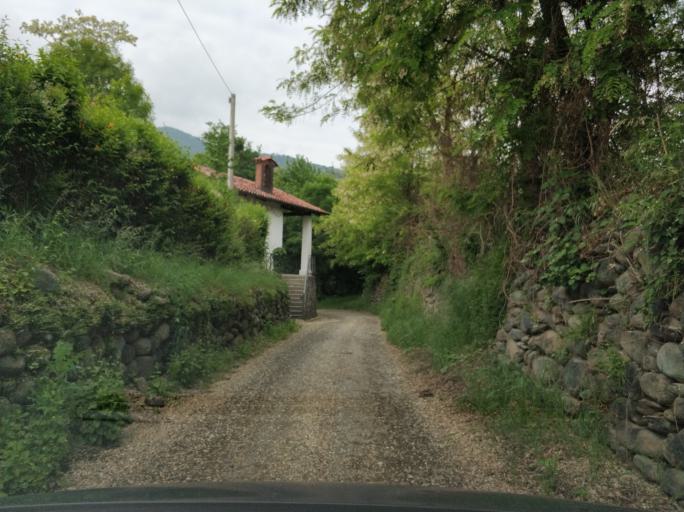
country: IT
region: Piedmont
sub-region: Provincia di Torino
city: Balangero
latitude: 45.2662
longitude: 7.5134
